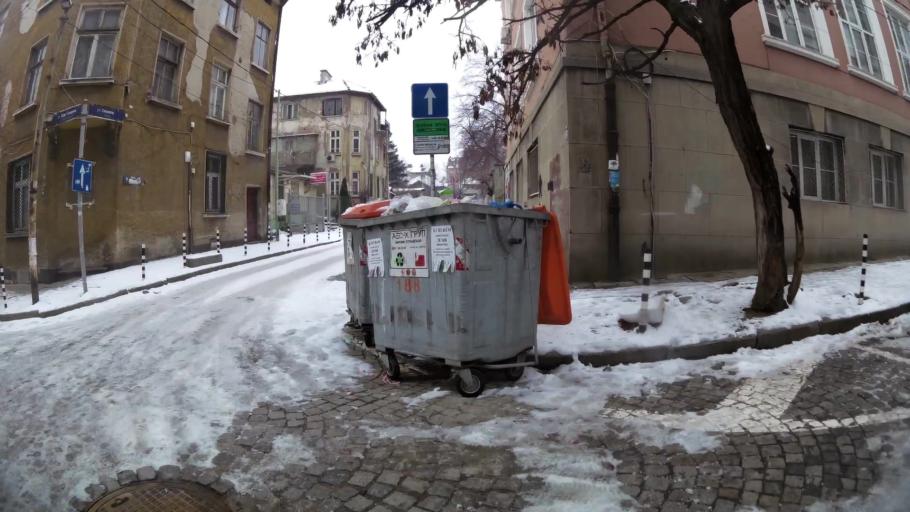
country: BG
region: Sofia-Capital
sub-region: Stolichna Obshtina
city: Sofia
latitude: 42.7073
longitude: 23.3206
